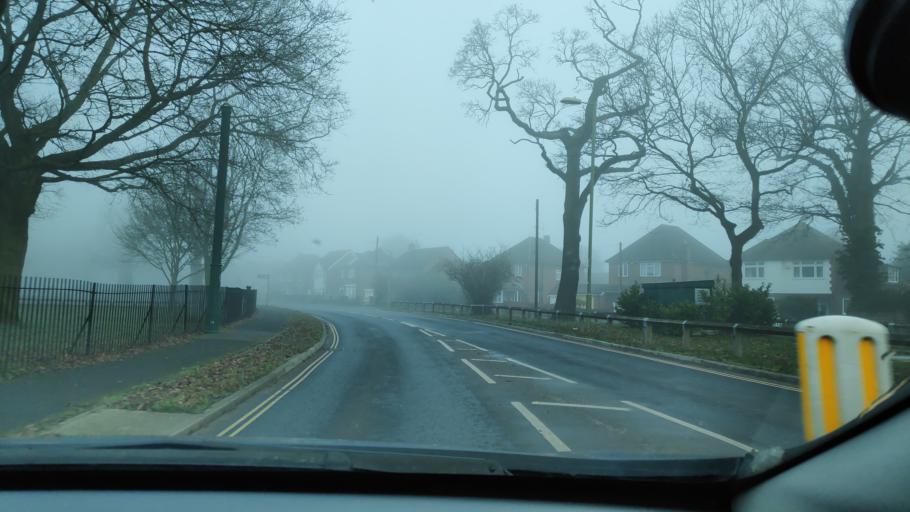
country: GB
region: England
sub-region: Hampshire
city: Farnborough
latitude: 51.2844
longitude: -0.7375
